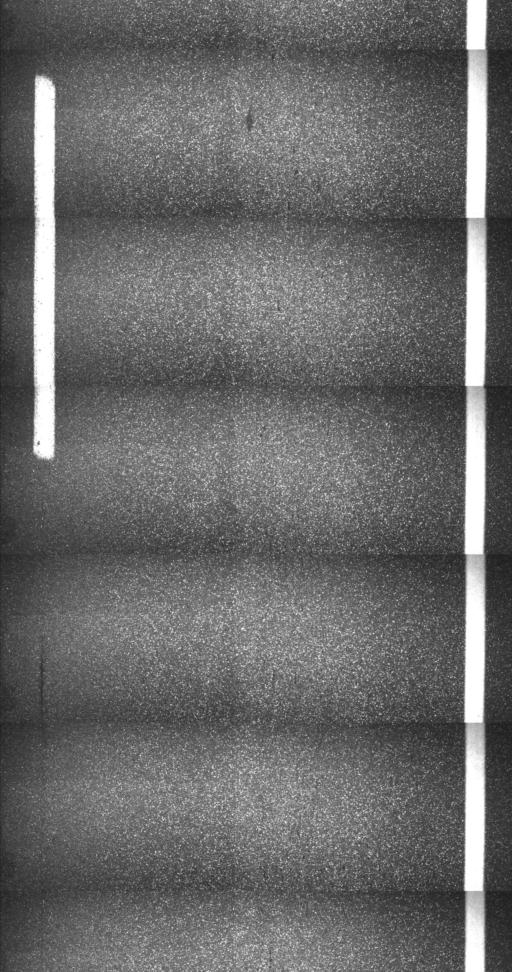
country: US
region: Vermont
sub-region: Washington County
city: Montpelier
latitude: 44.2233
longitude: -72.5856
